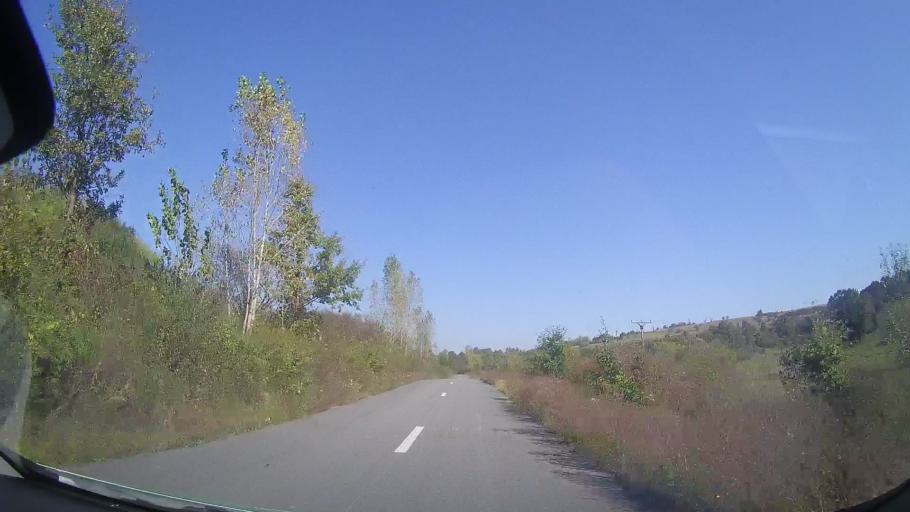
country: RO
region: Timis
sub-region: Comuna Bara
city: Bara
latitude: 45.8727
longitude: 21.8836
